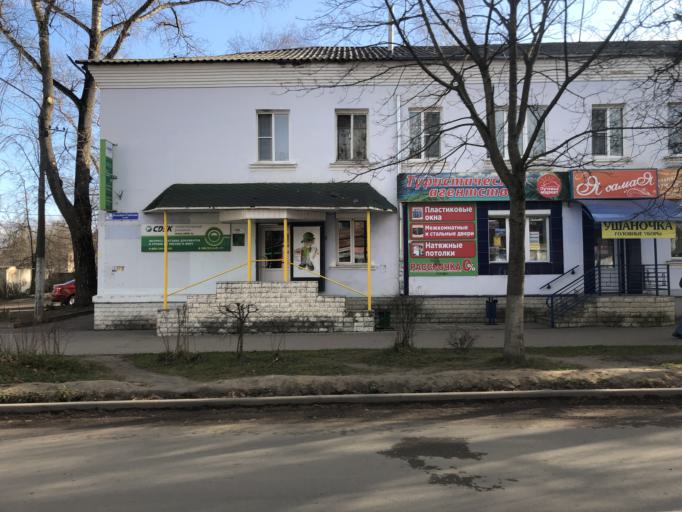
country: RU
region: Tverskaya
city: Rzhev
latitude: 56.2536
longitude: 34.3278
